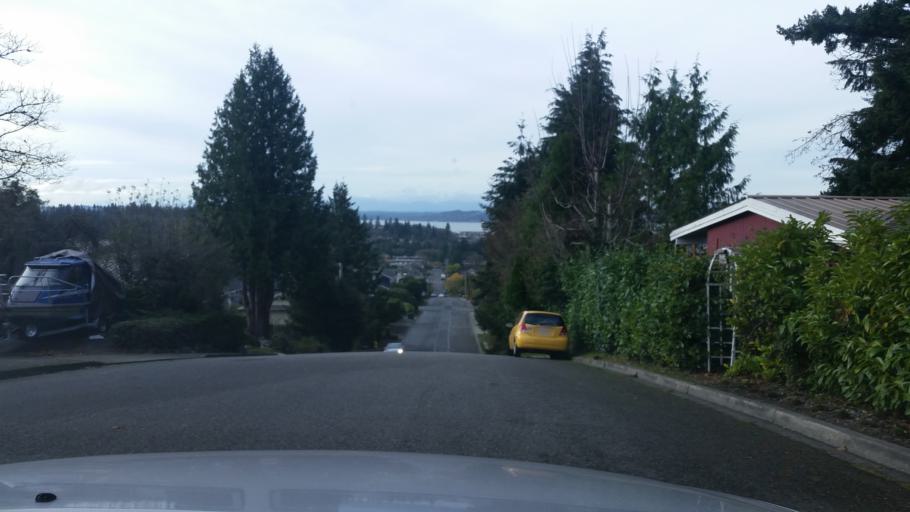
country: US
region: Washington
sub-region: Snohomish County
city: Edmonds
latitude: 47.8033
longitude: -122.3672
